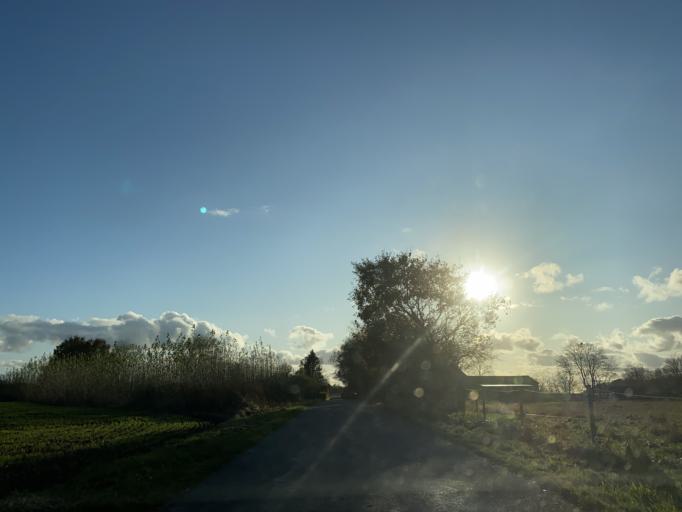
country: DK
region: Central Jutland
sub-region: Viborg Kommune
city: Bjerringbro
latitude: 56.3192
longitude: 9.7001
